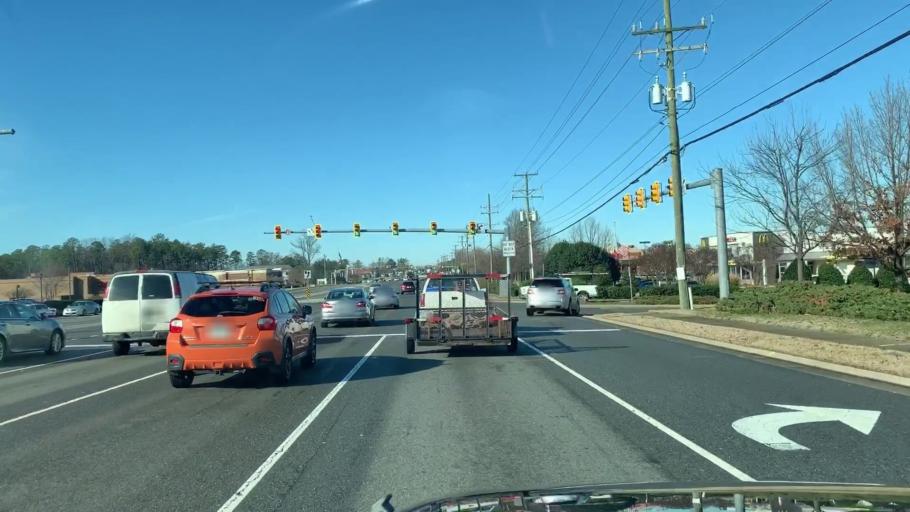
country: US
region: Virginia
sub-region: Henrico County
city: Short Pump
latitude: 37.6499
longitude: -77.6037
